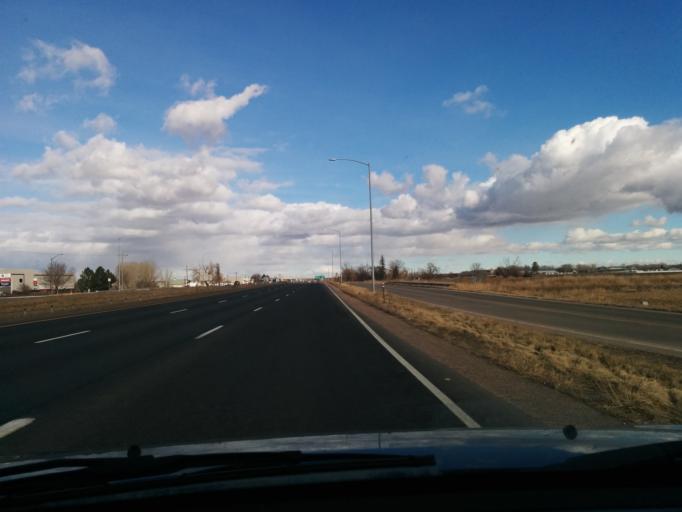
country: US
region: Colorado
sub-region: Larimer County
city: Fort Collins
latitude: 40.5692
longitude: -105.0011
